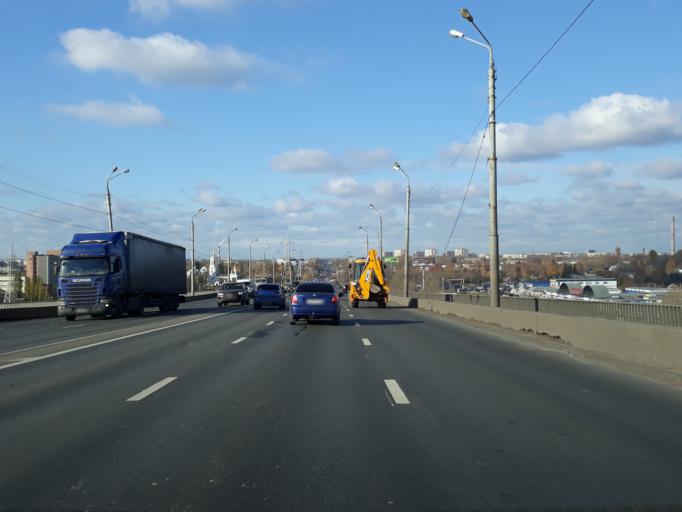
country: RU
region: Nizjnij Novgorod
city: Nizhniy Novgorod
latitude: 56.2520
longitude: 43.9443
